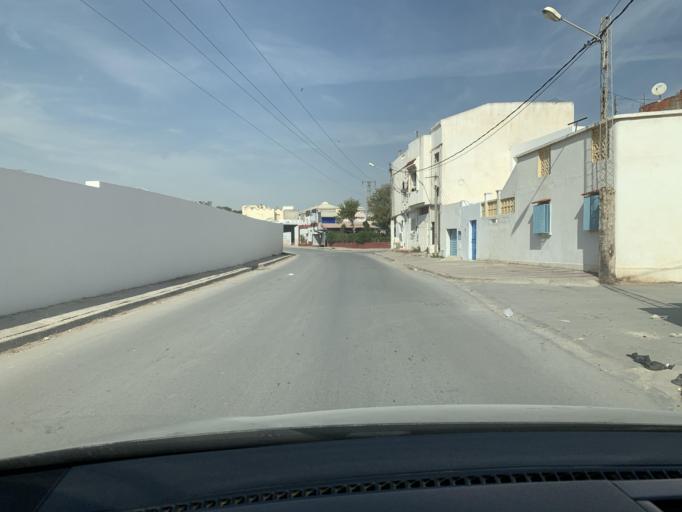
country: TN
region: Manouba
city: Manouba
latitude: 36.8211
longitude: 10.1170
